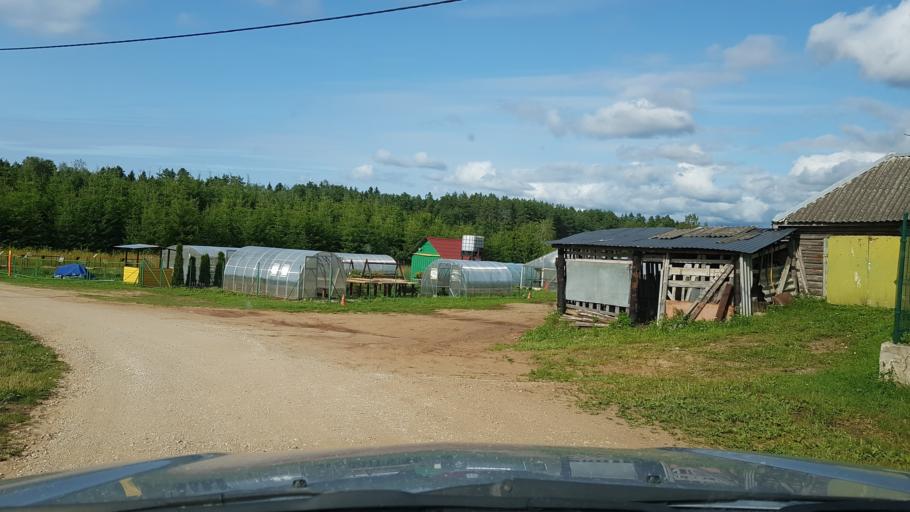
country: EE
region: Ida-Virumaa
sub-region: Narva-Joesuu linn
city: Narva-Joesuu
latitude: 59.4109
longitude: 28.0712
